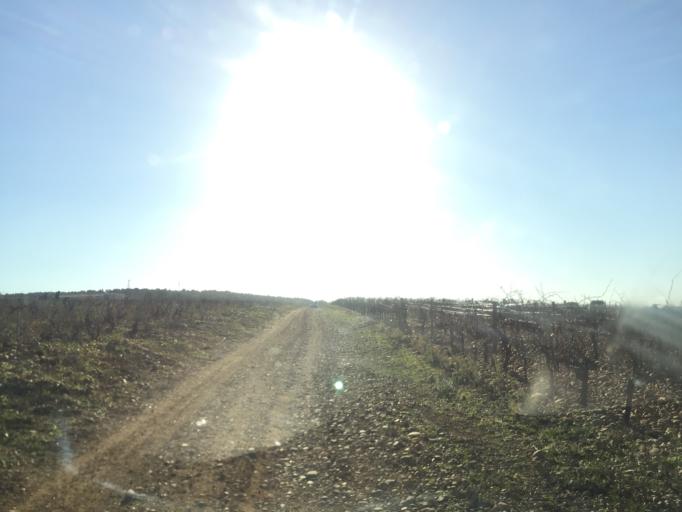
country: FR
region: Provence-Alpes-Cote d'Azur
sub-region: Departement du Vaucluse
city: Bedarrides
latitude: 44.0297
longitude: 4.8895
